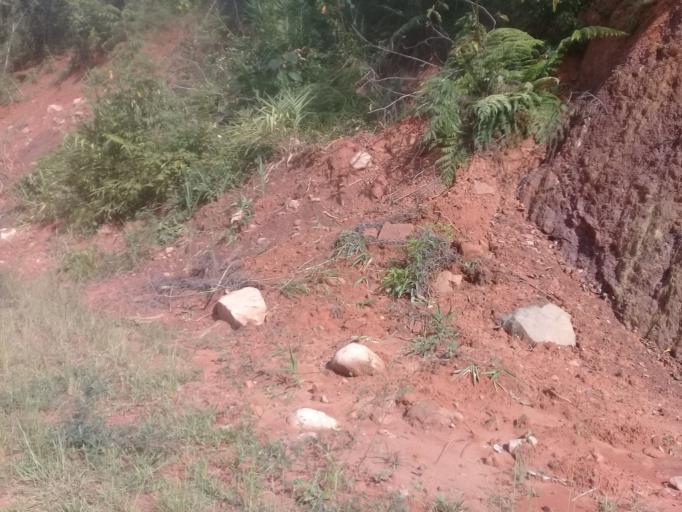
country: VN
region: Huyen Dien Bien
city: Thi Tran Muong Cha
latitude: 21.7457
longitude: 102.8368
